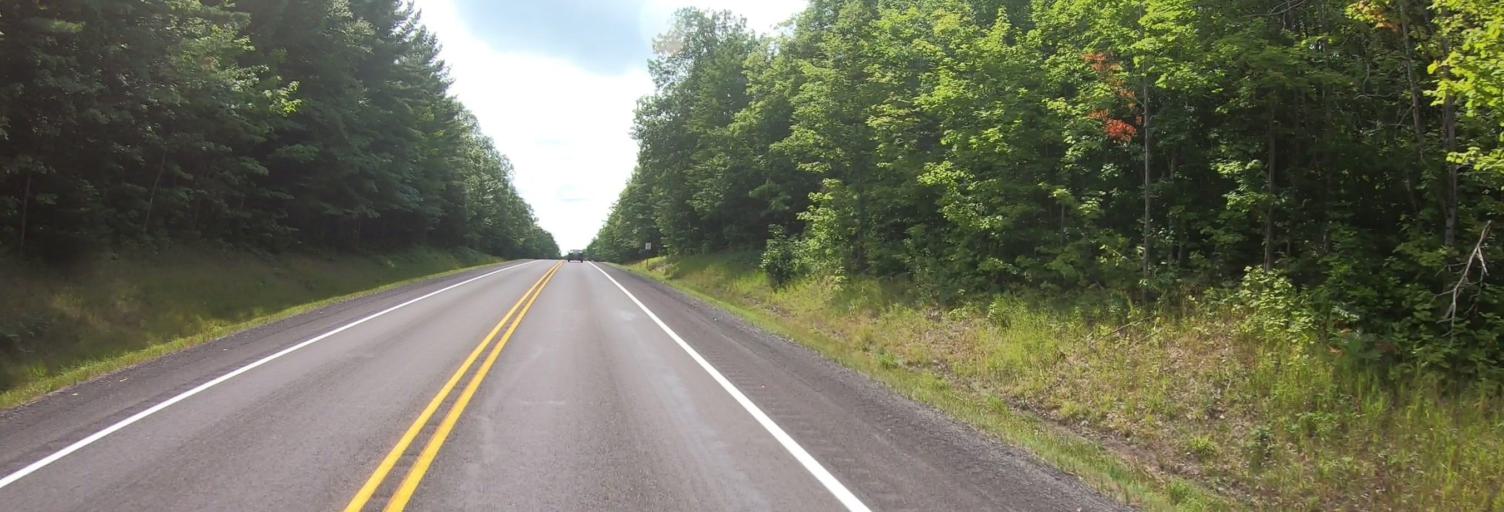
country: US
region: Michigan
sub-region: Houghton County
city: Hancock
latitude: 47.0303
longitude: -88.7206
